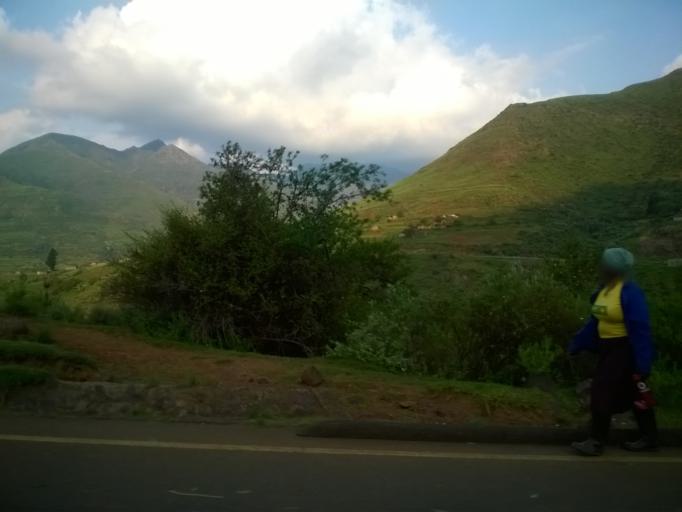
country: LS
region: Butha-Buthe
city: Butha-Buthe
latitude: -29.0456
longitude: 28.3105
